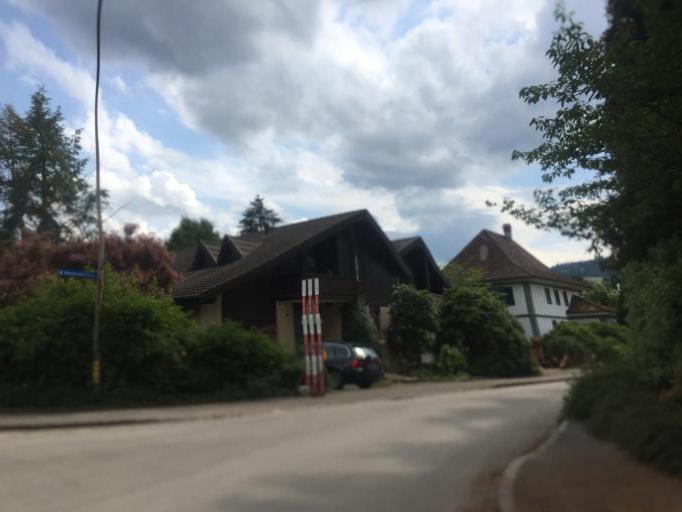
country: CH
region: Bern
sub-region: Bern-Mittelland District
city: Muri
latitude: 46.9291
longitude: 7.4754
